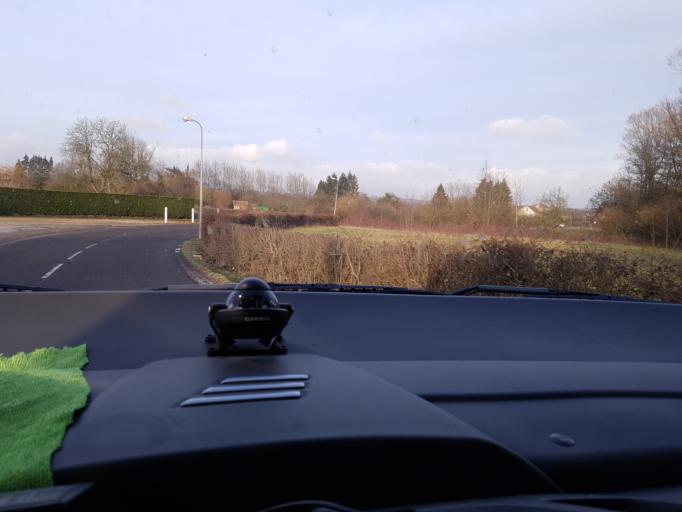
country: FR
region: Champagne-Ardenne
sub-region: Departement des Ardennes
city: Warcq
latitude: 49.7660
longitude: 4.6742
